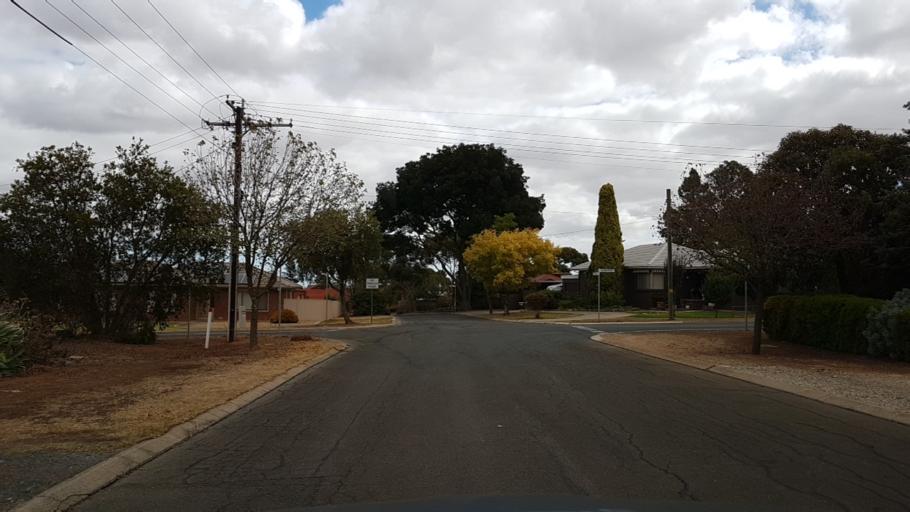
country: AU
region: South Australia
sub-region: Gawler
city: Gawler
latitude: -34.6041
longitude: 138.7616
